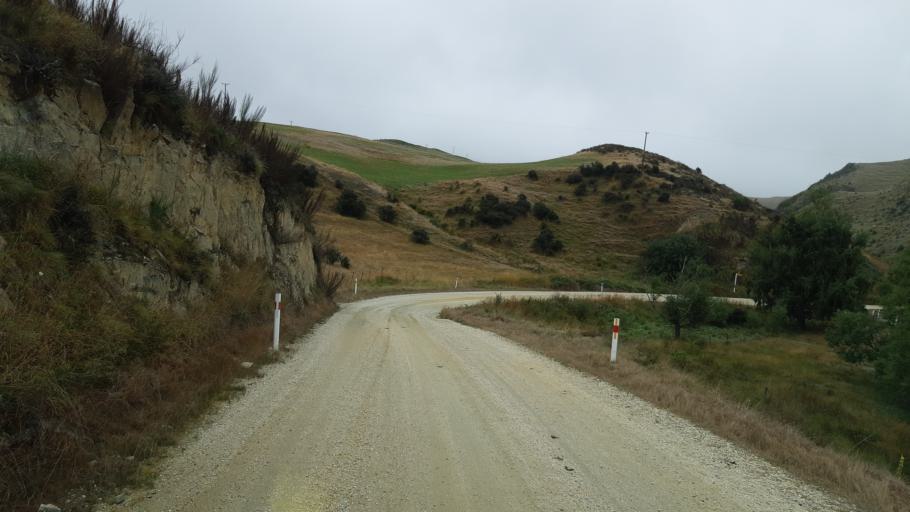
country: NZ
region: Otago
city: Oamaru
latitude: -44.9736
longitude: 170.5150
